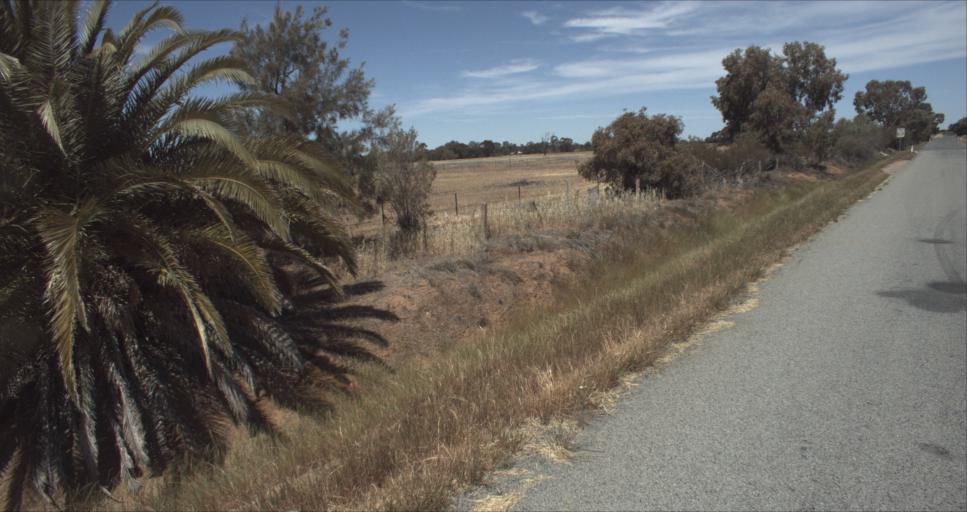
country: AU
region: New South Wales
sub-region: Leeton
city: Leeton
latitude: -34.6015
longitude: 146.4155
